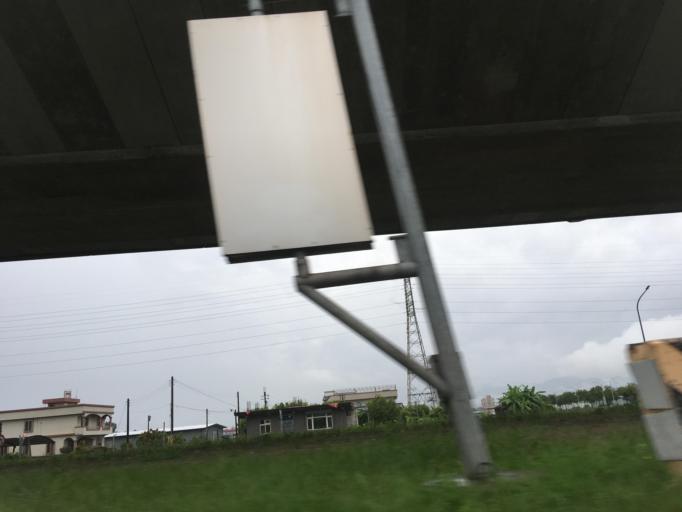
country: TW
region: Taiwan
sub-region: Yilan
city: Yilan
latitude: 24.6926
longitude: 121.7911
